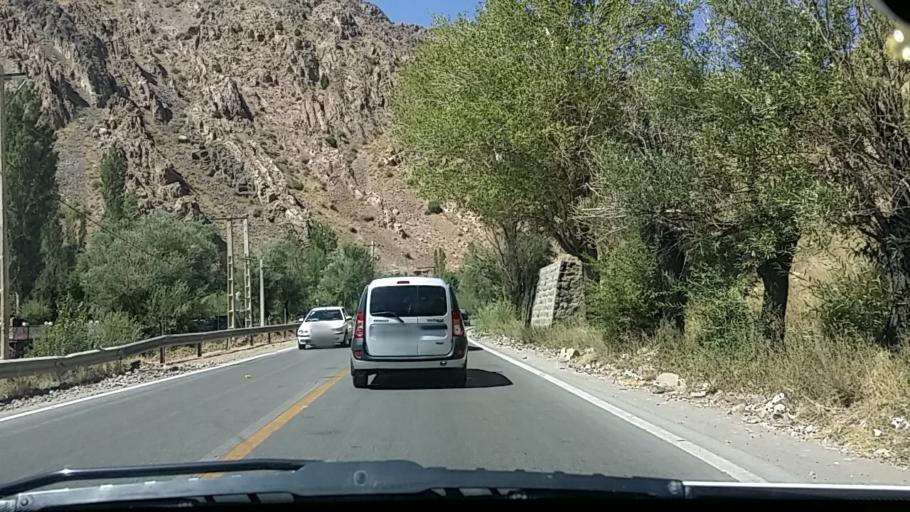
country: IR
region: Tehran
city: Tajrish
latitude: 36.0576
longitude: 51.3111
